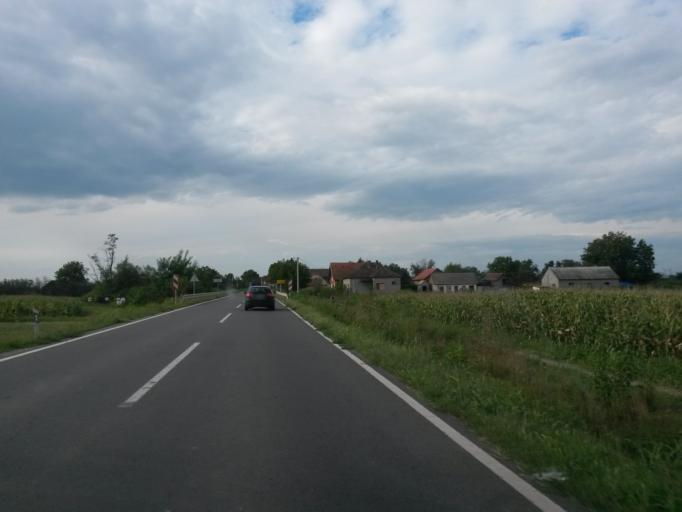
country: HR
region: Vukovarsko-Srijemska
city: Markusica
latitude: 45.3851
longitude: 18.6962
